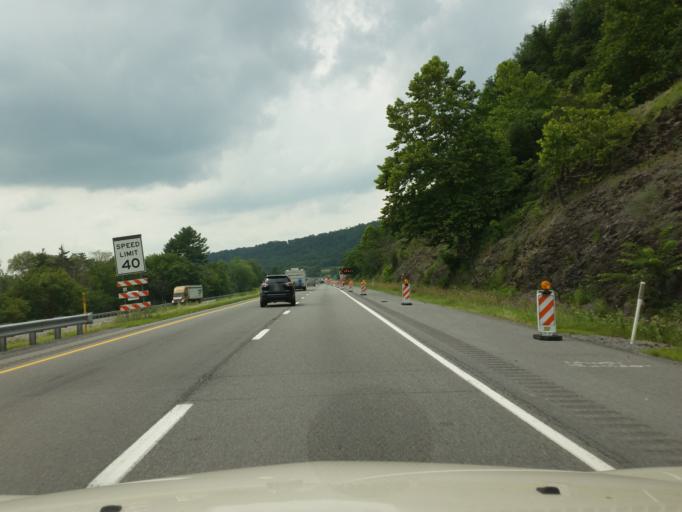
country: US
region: Pennsylvania
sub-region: Perry County
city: Newport
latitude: 40.5652
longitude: -77.1940
